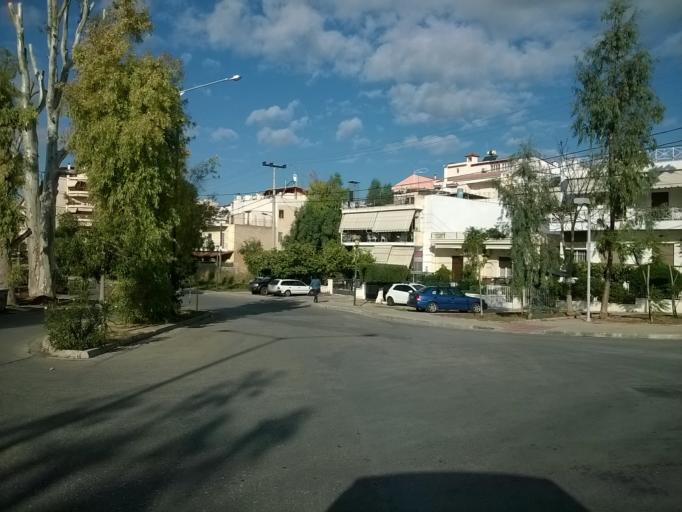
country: GR
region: Attica
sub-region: Nomarchia Athinas
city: Agios Dimitrios
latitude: 37.9189
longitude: 23.7401
